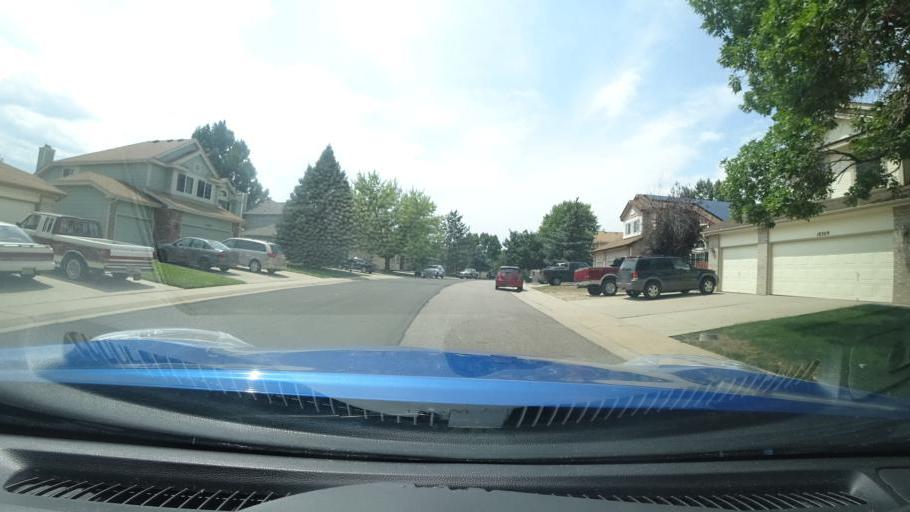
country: US
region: Colorado
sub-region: Adams County
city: Aurora
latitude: 39.6715
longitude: -104.7735
